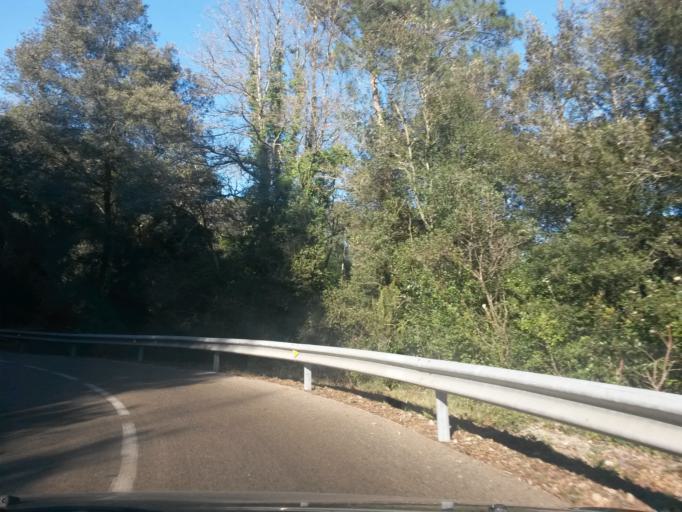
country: ES
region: Catalonia
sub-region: Provincia de Girona
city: Angles
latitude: 41.9962
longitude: 2.6711
